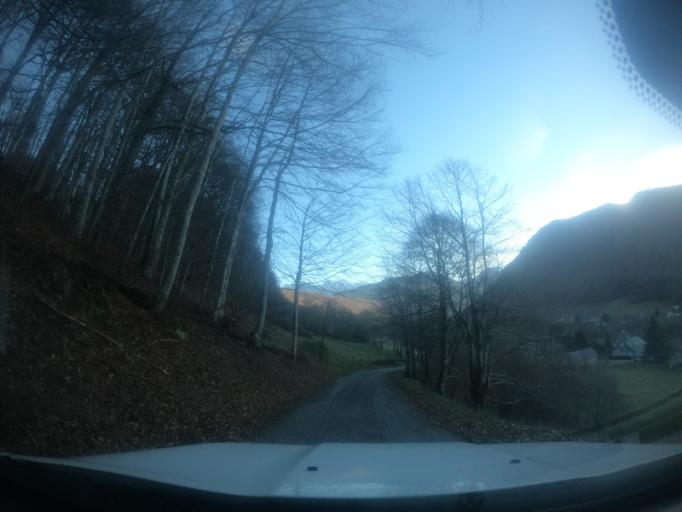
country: FR
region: Midi-Pyrenees
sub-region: Departement des Hautes-Pyrenees
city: Campan
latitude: 42.9769
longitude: 0.2347
